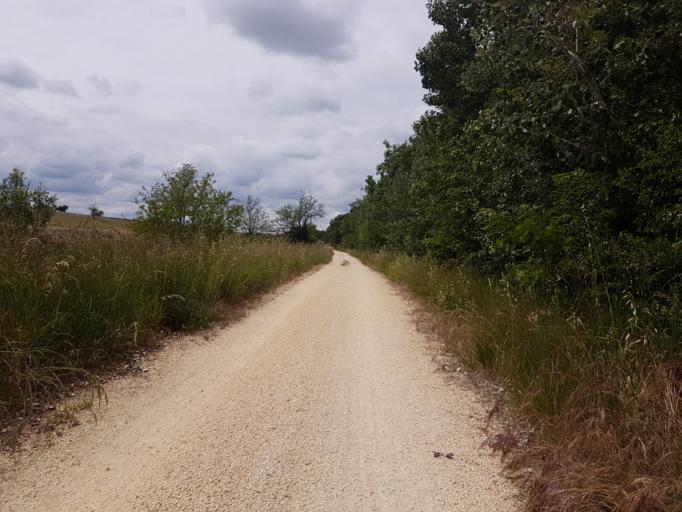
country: FR
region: Languedoc-Roussillon
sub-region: Departement du Gard
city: Aramon
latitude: 43.9026
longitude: 4.7048
